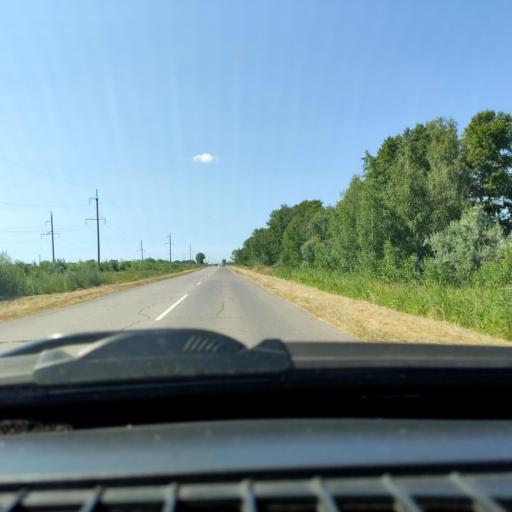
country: RU
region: Samara
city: Tol'yatti
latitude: 53.7293
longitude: 49.4141
